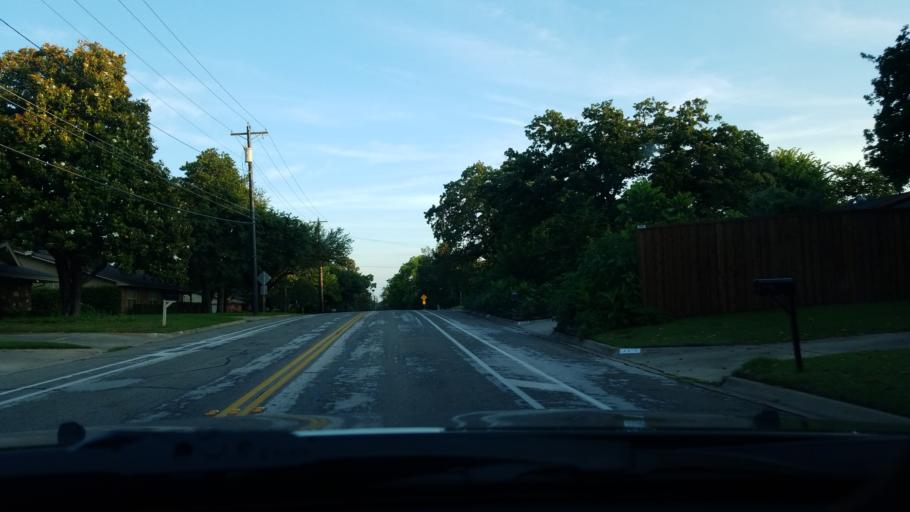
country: US
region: Texas
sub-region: Denton County
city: Denton
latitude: 33.2410
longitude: -97.1067
